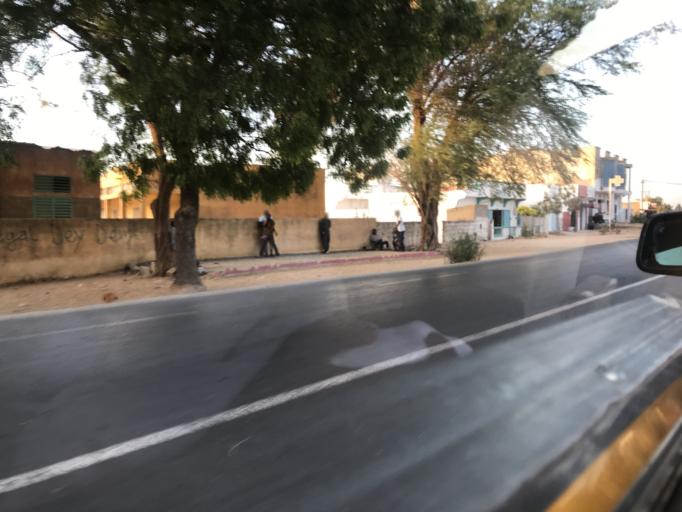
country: SN
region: Saint-Louis
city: Saint-Louis
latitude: 16.0407
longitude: -16.4429
